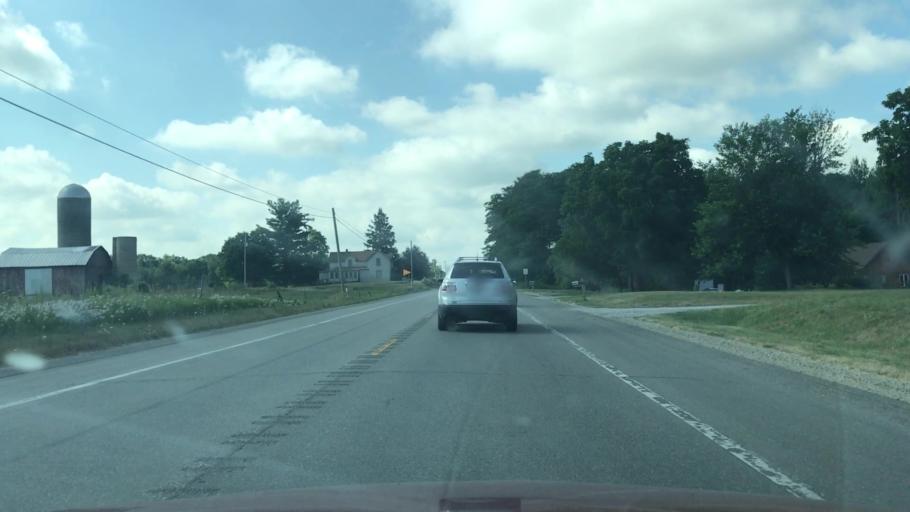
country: US
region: Michigan
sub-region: Kent County
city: Kent City
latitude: 43.2962
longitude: -85.8107
